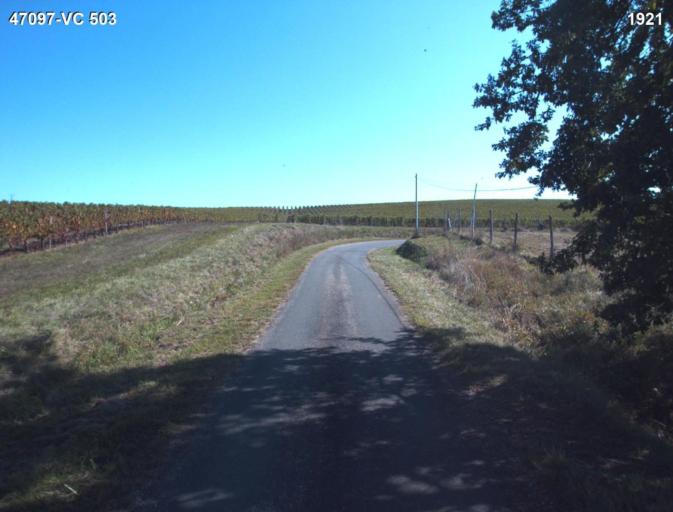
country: FR
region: Aquitaine
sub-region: Departement du Lot-et-Garonne
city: Port-Sainte-Marie
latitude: 44.2080
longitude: 0.3703
